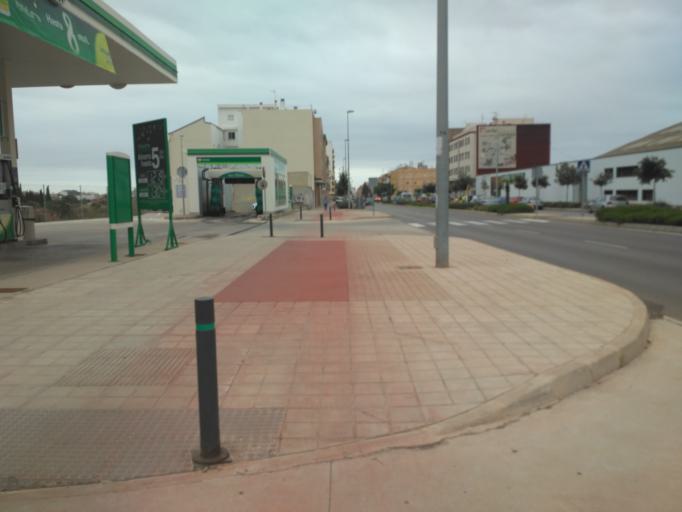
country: ES
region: Valencia
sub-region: Provincia de Castello
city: Castello de la Plana
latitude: 39.9883
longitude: -0.0659
